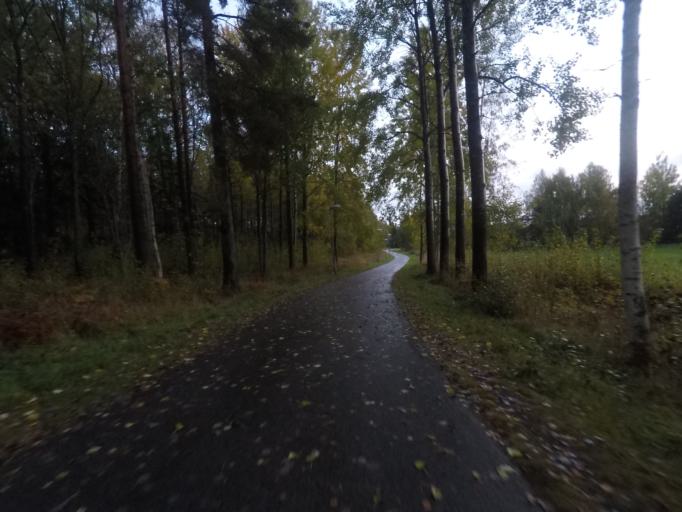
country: SE
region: OErebro
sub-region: Karlskoga Kommun
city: Karlskoga
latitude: 59.3125
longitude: 14.4864
